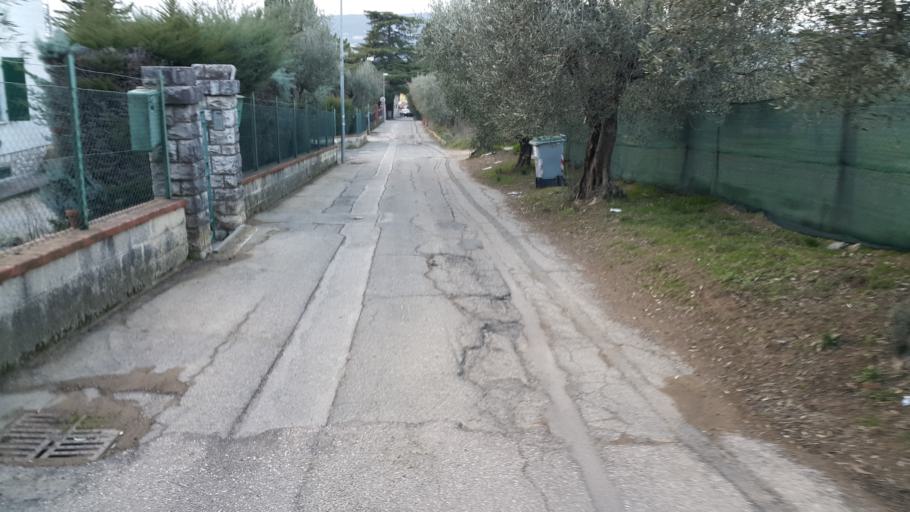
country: IT
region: Umbria
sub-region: Provincia di Perugia
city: Perugia
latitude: 43.0896
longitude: 12.3725
